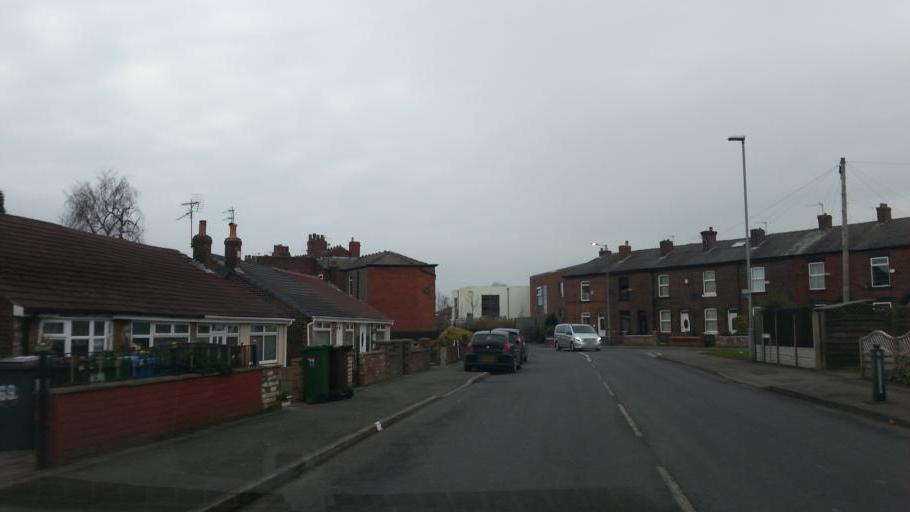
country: GB
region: England
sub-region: Borough of Tameside
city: Denton
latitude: 53.4580
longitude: -2.1229
